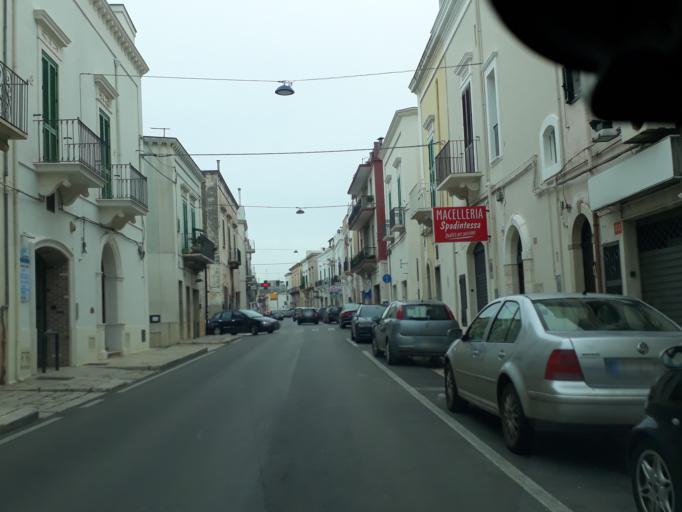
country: IT
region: Apulia
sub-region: Provincia di Brindisi
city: Fasano
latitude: 40.8378
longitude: 17.3604
